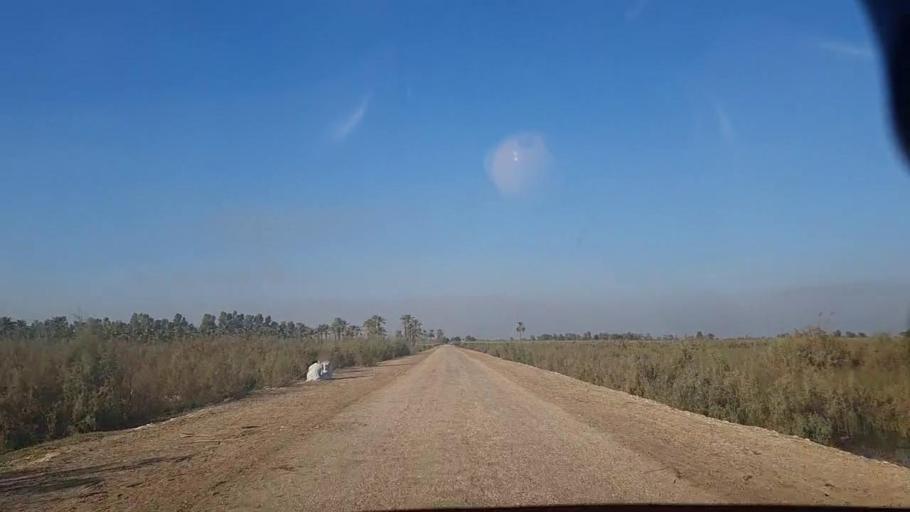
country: PK
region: Sindh
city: Sobhadero
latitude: 27.4061
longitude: 68.4220
